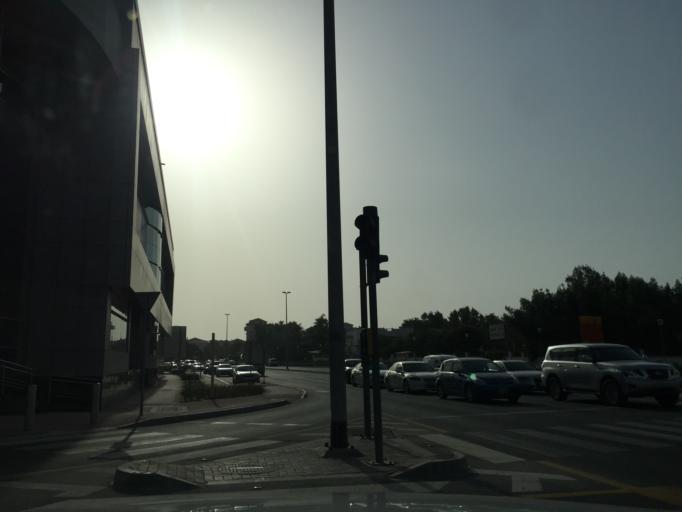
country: AE
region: Dubai
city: Dubai
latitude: 25.1045
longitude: 55.1675
